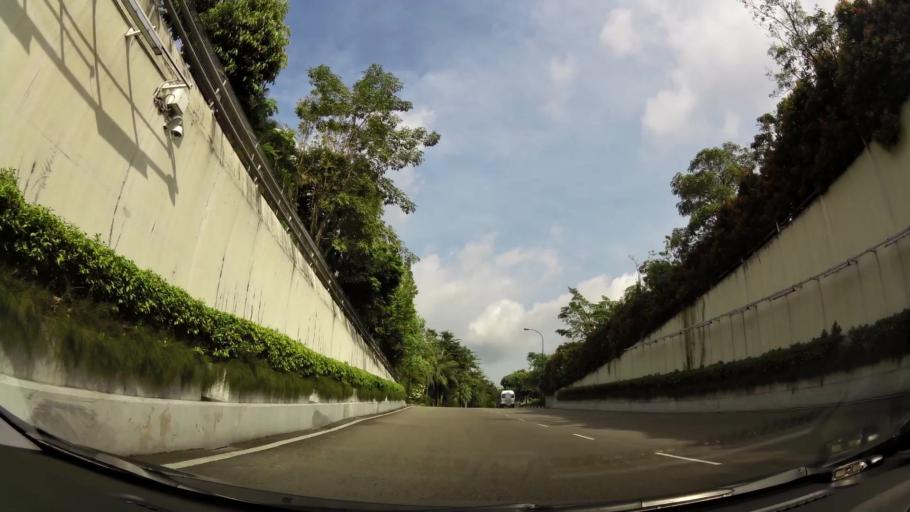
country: SG
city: Singapore
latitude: 1.2554
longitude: 103.8242
